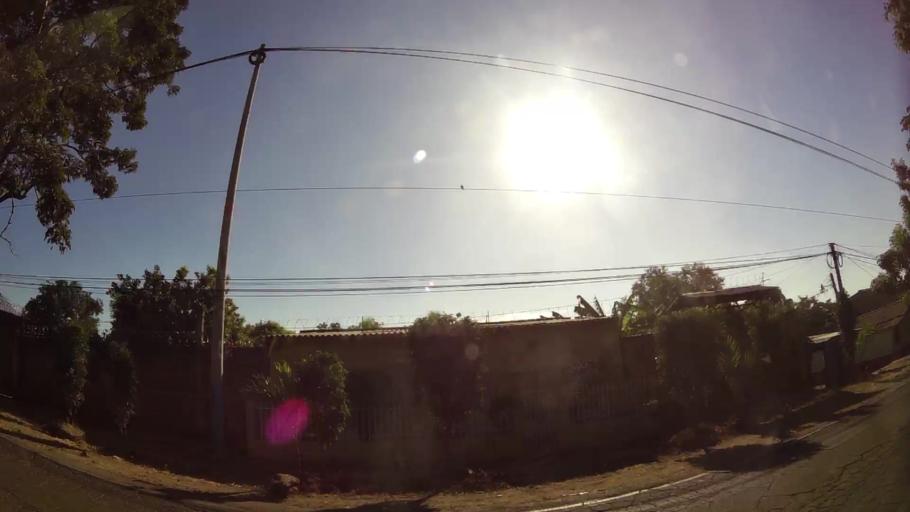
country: SV
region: Sonsonate
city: Sonzacate
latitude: 13.7429
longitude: -89.7088
